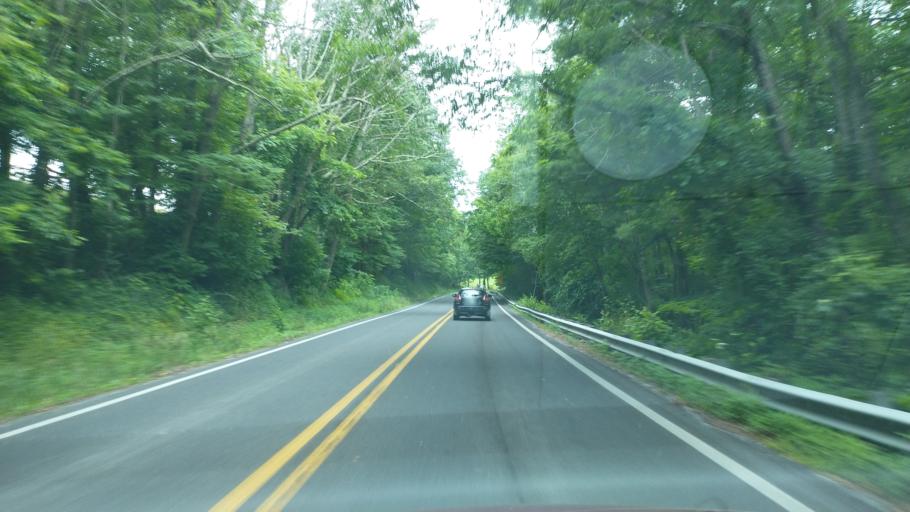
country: US
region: West Virginia
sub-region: Mercer County
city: Athens
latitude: 37.4092
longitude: -81.0246
